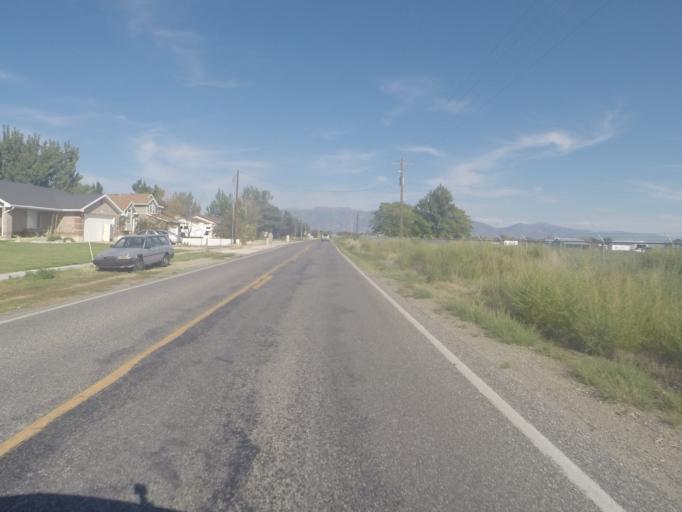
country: US
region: Utah
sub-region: Davis County
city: West Point
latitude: 41.0892
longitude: -112.1110
